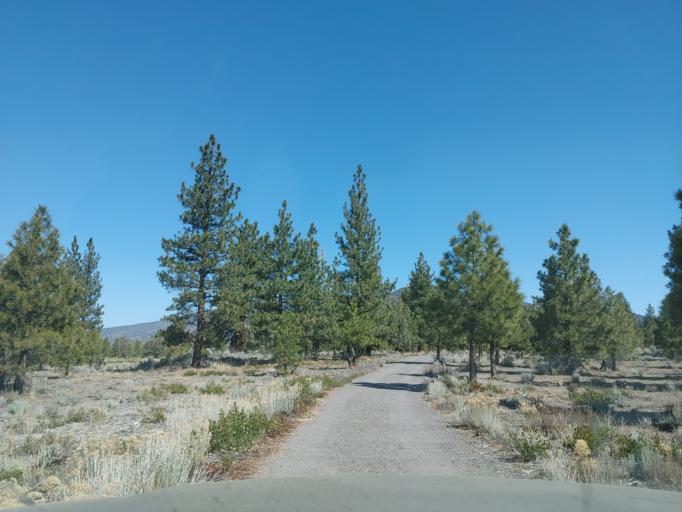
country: US
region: California
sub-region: Siskiyou County
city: Weed
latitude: 41.5454
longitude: -122.2324
